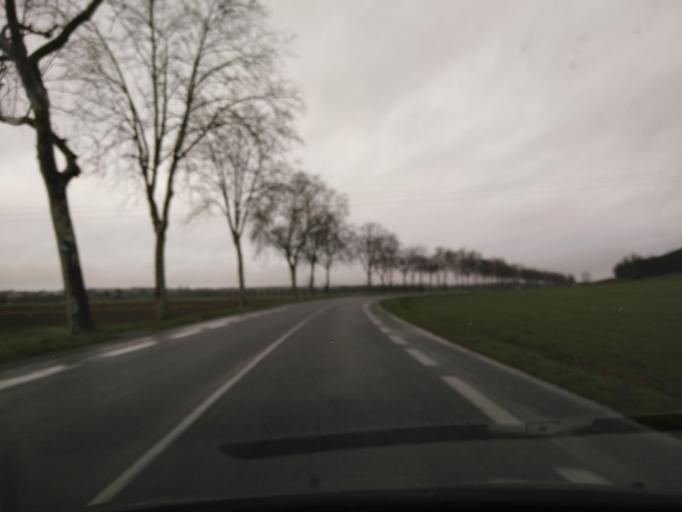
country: FR
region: Midi-Pyrenees
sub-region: Departement de la Haute-Garonne
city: Rieux-Volvestre
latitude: 43.2383
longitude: 1.2040
